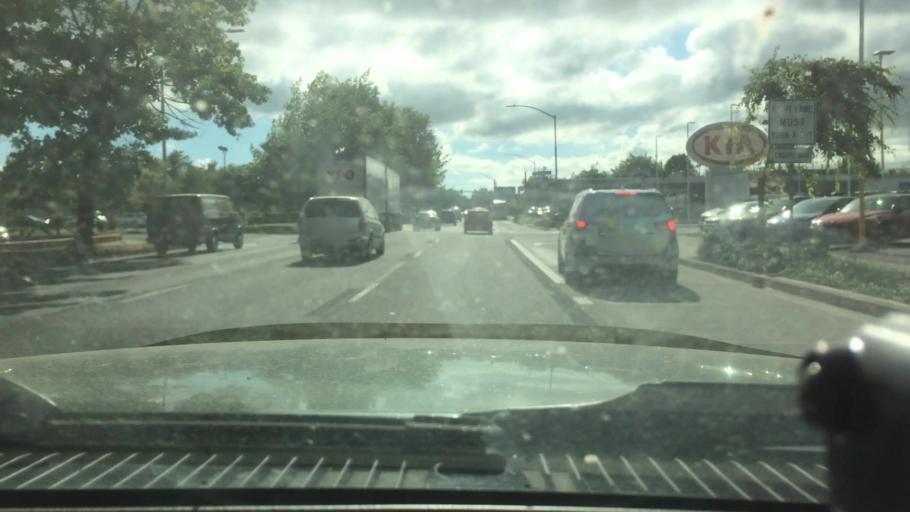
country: US
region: Oregon
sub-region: Lane County
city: Eugene
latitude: 44.0521
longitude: -123.1208
